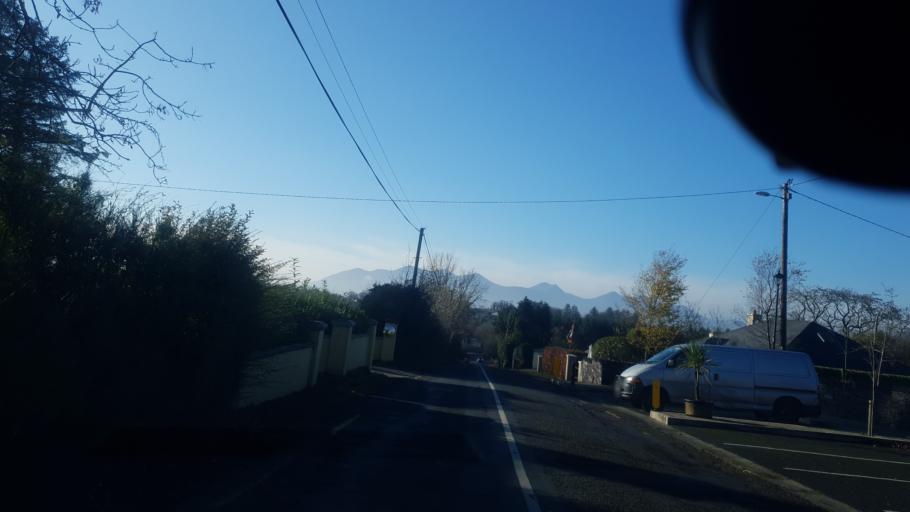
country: IE
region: Munster
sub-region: Ciarrai
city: Cill Airne
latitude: 52.0966
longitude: -9.4724
